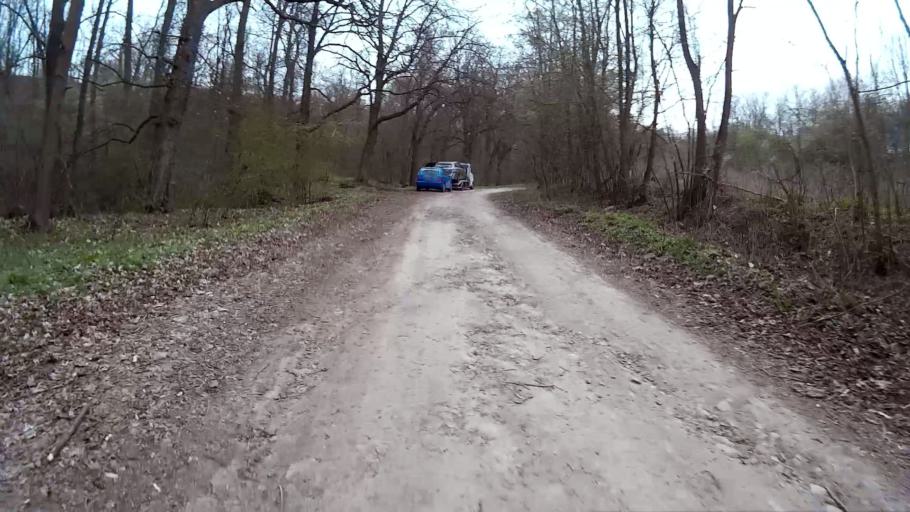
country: CZ
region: South Moravian
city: Ivancice
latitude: 49.0885
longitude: 16.3515
